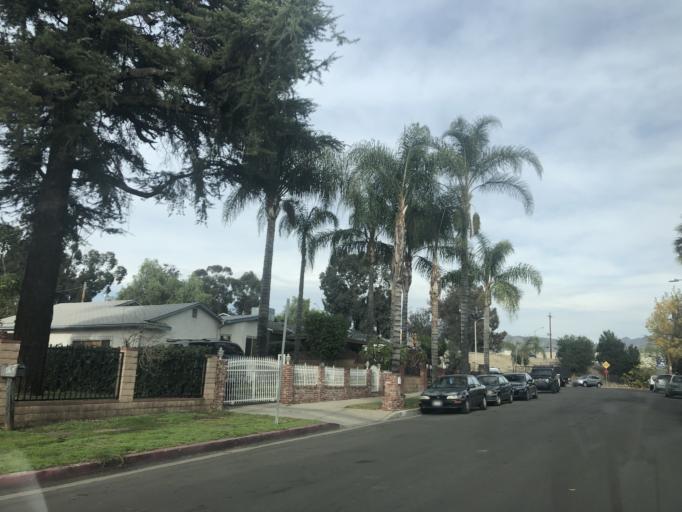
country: US
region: California
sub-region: Los Angeles County
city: San Fernando
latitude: 34.2700
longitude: -118.4292
